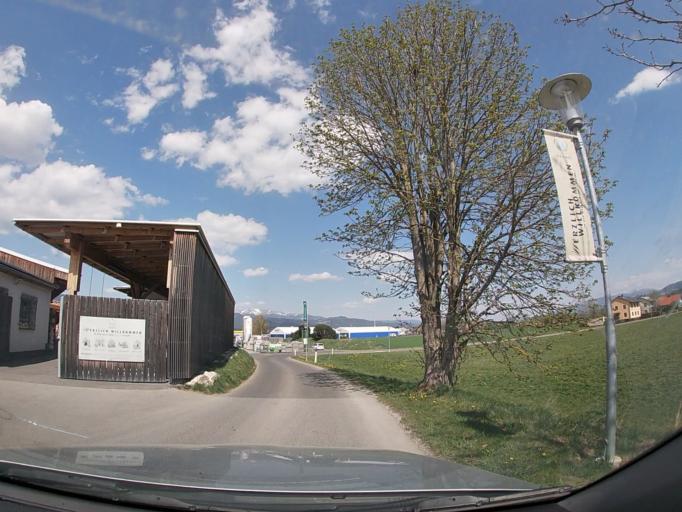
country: AT
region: Styria
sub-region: Politischer Bezirk Murtal
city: Weisskirchen in Steiermark
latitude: 47.1577
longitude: 14.7339
